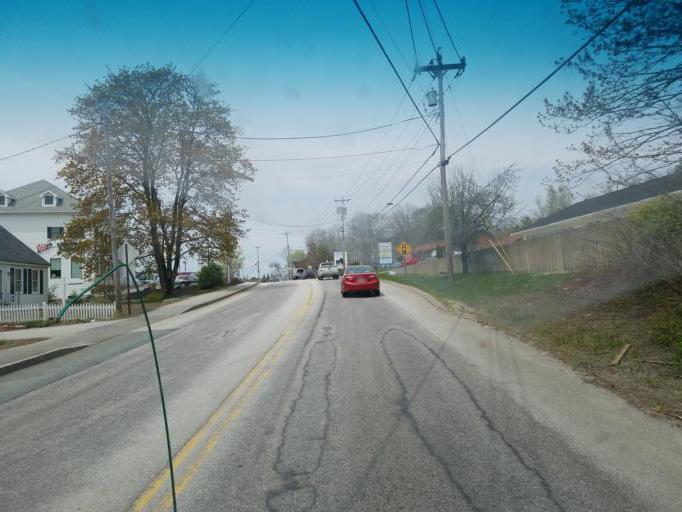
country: US
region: Maine
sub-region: Hancock County
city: Ellsworth
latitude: 44.5489
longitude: -68.4250
